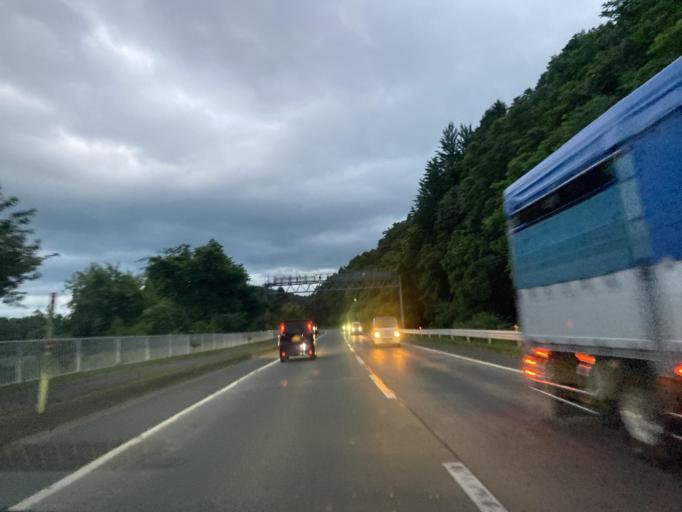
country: JP
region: Iwate
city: Morioka-shi
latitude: 39.9211
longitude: 141.1957
